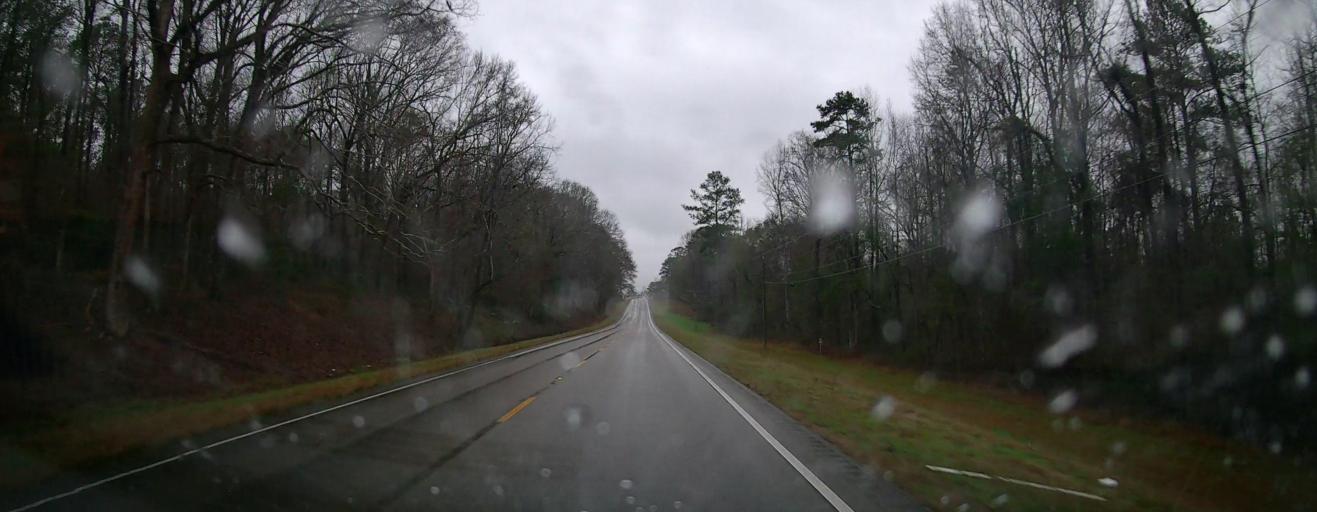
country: US
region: Alabama
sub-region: Autauga County
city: Prattville
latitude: 32.4859
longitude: -86.5384
